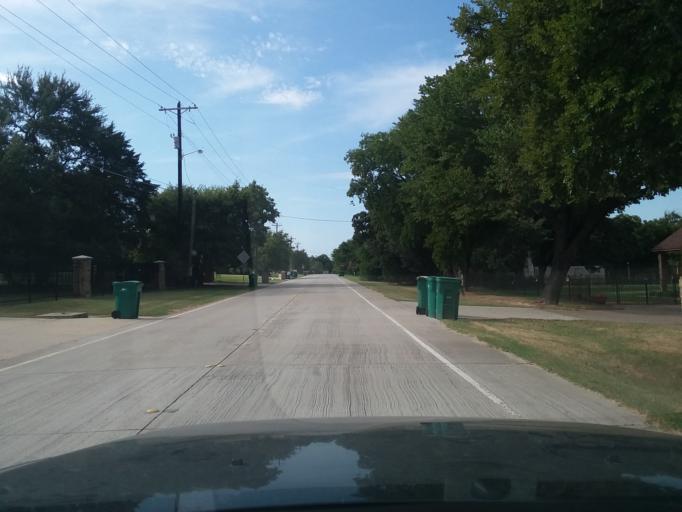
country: US
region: Texas
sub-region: Denton County
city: Double Oak
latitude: 33.0621
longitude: -97.1143
